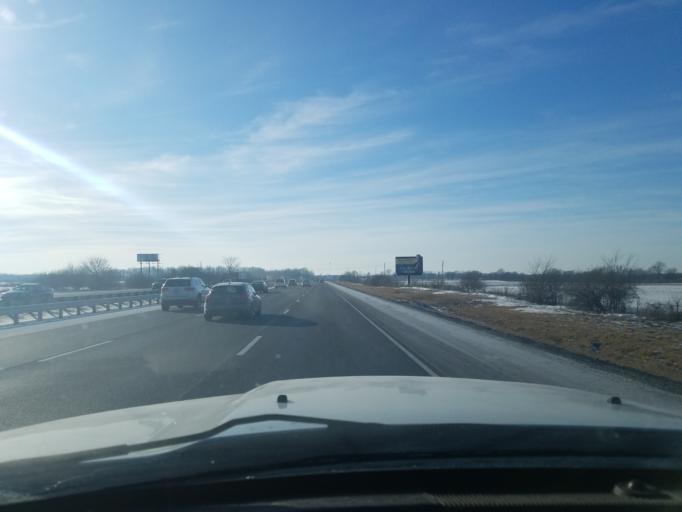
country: US
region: Indiana
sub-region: Hancock County
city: Fortville
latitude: 39.9925
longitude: -85.8596
